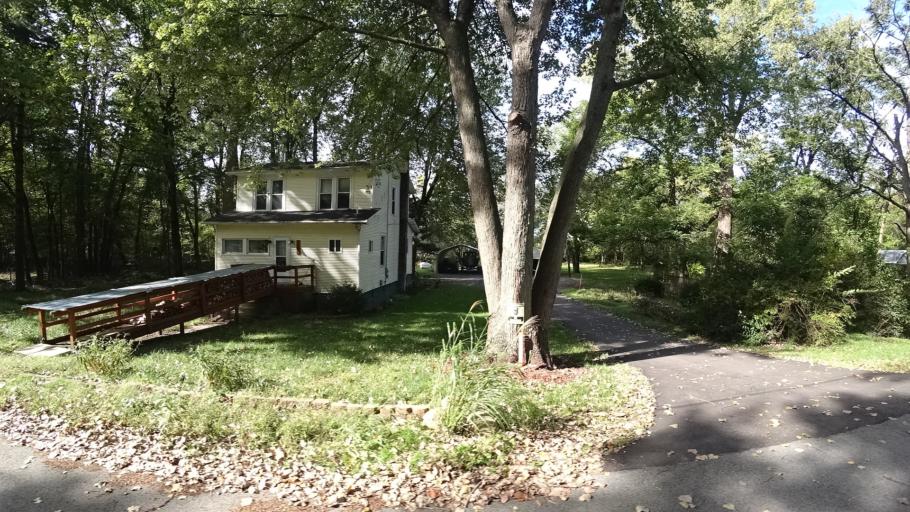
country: US
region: Indiana
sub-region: LaPorte County
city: Michigan City
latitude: 41.7221
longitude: -86.8757
